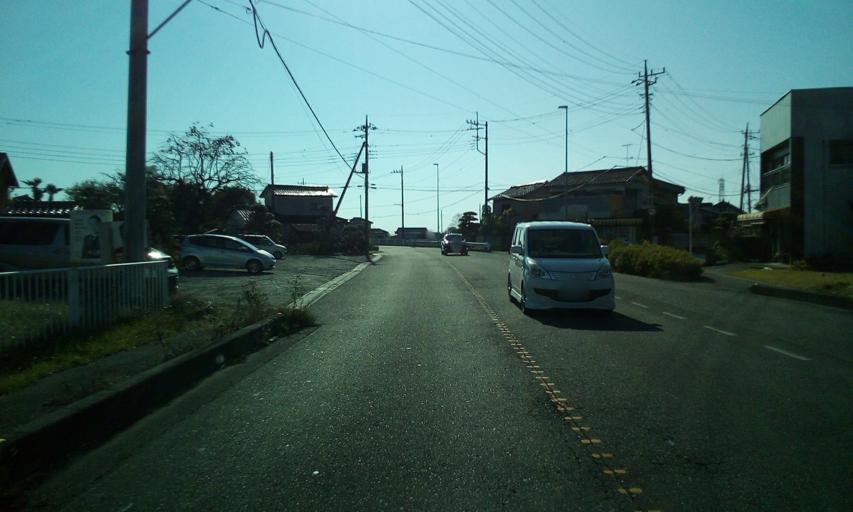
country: JP
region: Ibaraki
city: Sakai
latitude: 36.0805
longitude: 139.7761
